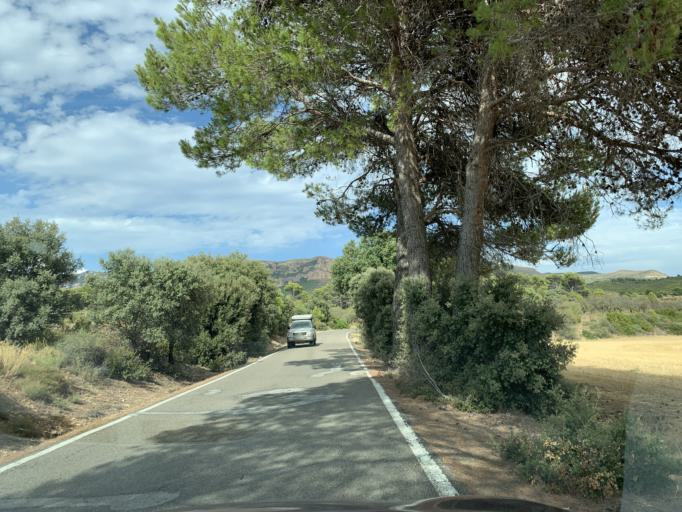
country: ES
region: Aragon
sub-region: Provincia de Zaragoza
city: Santa Eulalia de Gallego
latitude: 42.3152
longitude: -0.7327
